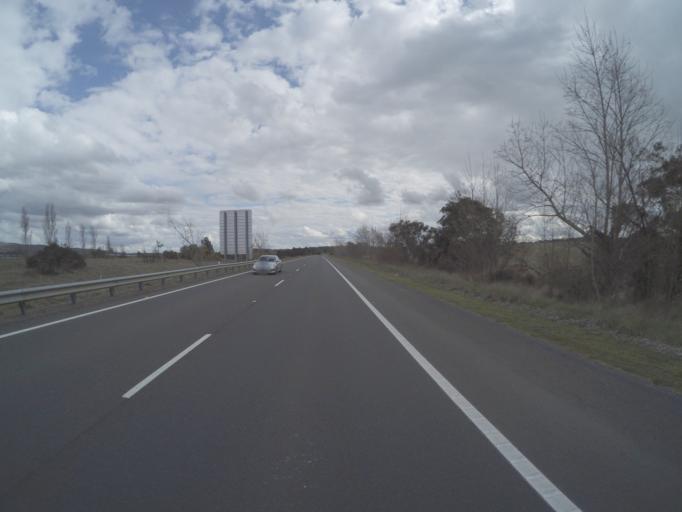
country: AU
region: New South Wales
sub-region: Goulburn Mulwaree
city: Goulburn
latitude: -34.8018
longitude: 149.6096
